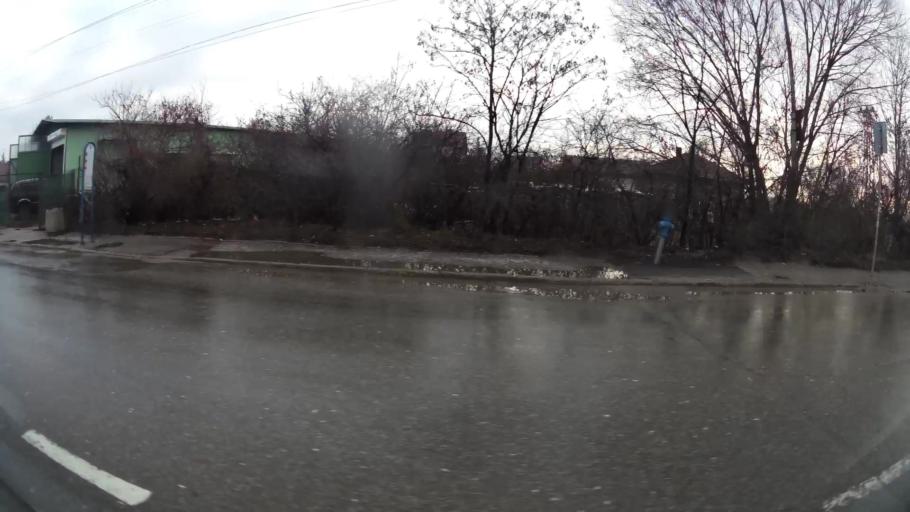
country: BG
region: Sofia-Capital
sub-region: Stolichna Obshtina
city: Sofia
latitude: 42.7339
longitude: 23.3434
